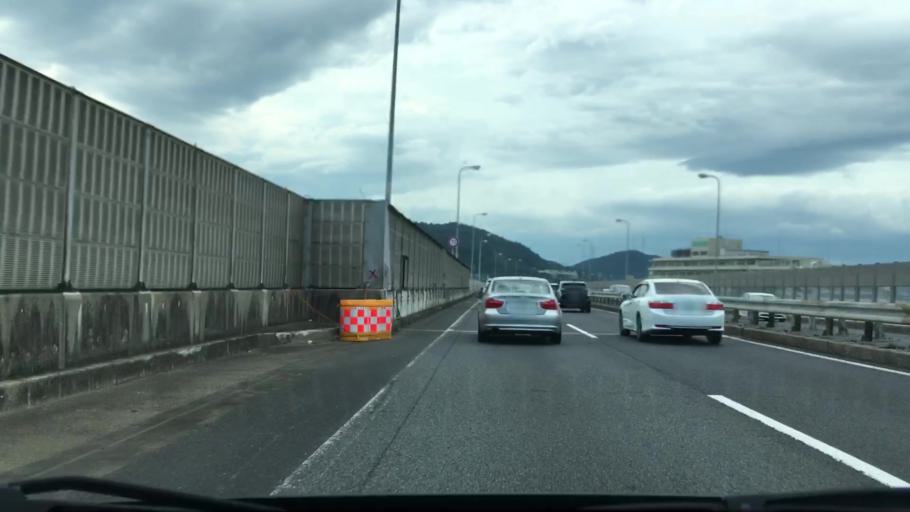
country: JP
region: Hyogo
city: Kakogawacho-honmachi
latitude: 34.7874
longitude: 134.7749
